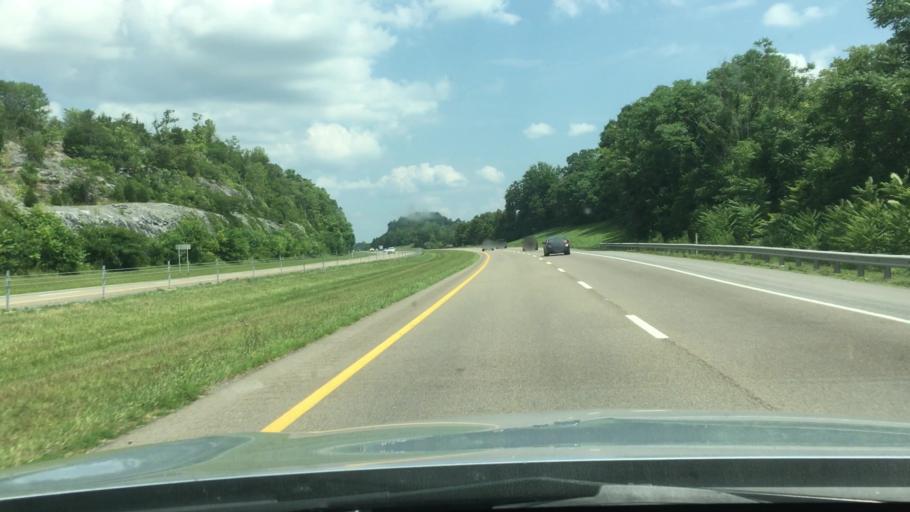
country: US
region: Tennessee
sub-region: Carter County
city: Pine Crest
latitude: 36.2531
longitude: -82.3237
